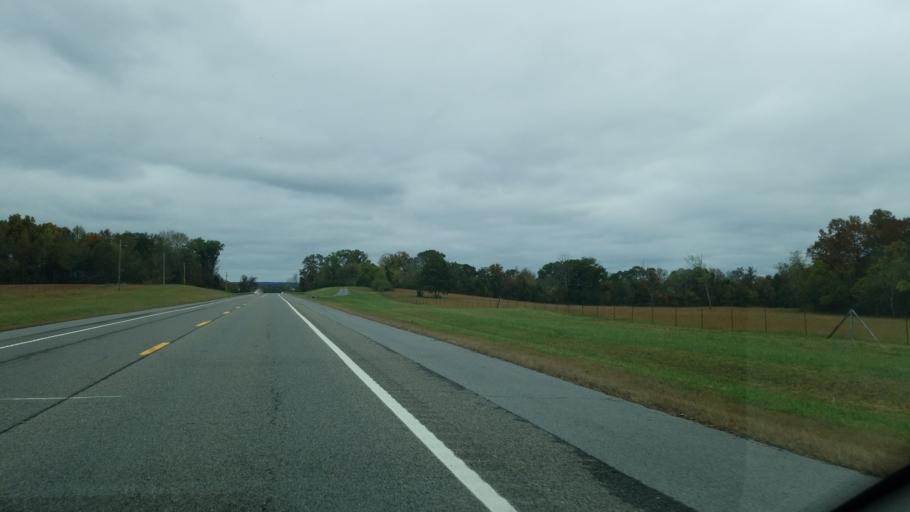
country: US
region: Tennessee
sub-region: Rhea County
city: Graysville
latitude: 35.4033
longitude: -85.0149
